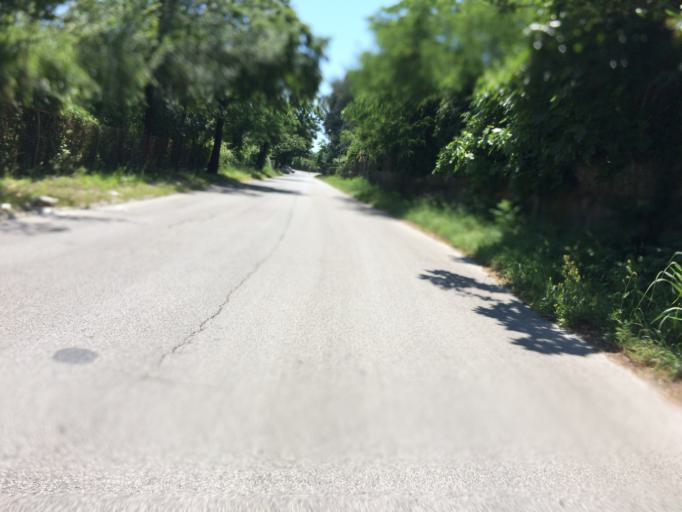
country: IT
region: Tuscany
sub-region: Provincia di Massa-Carrara
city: Massa
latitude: 44.0346
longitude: 10.1226
